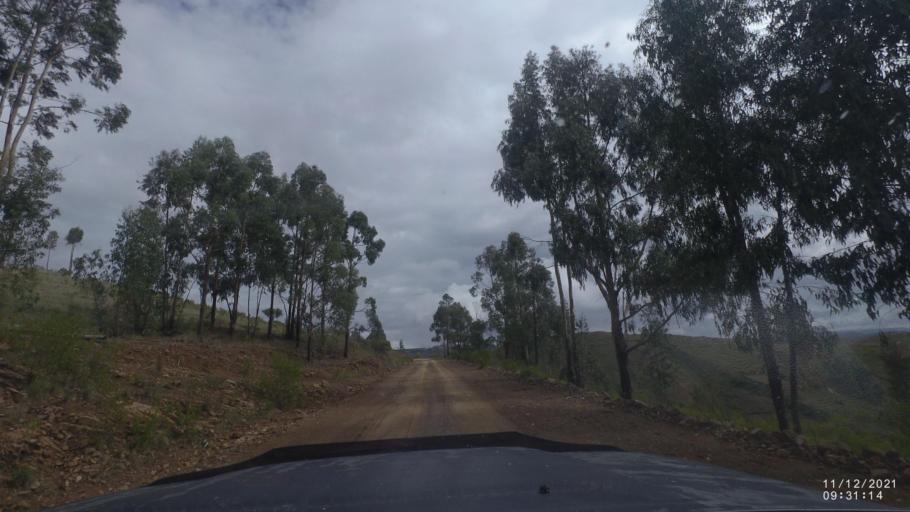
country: BO
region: Cochabamba
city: Tarata
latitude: -17.8541
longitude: -65.9883
